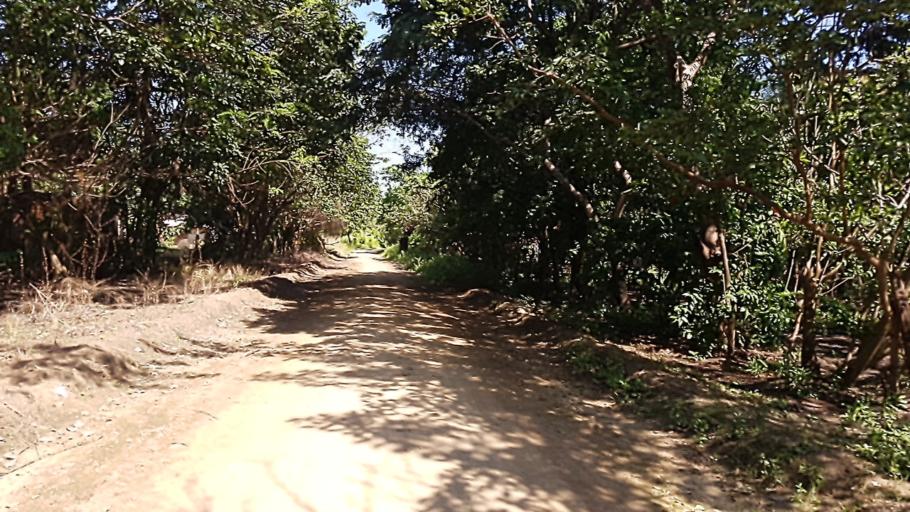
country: NI
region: Rivas
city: Belen
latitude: 11.5486
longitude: -85.8984
